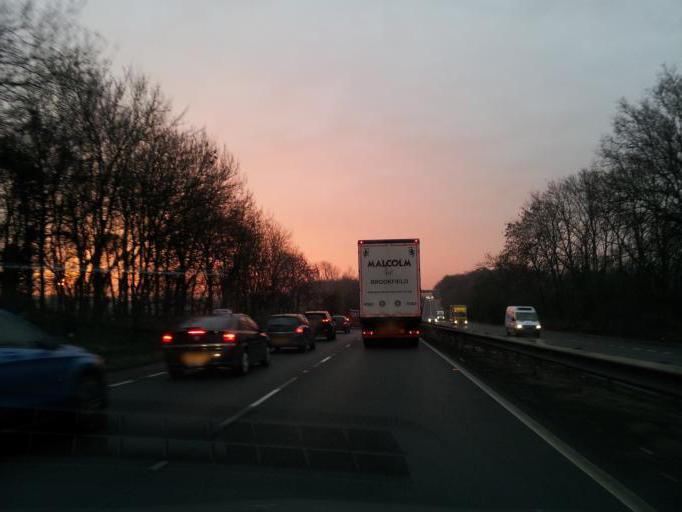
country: GB
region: England
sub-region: Peterborough
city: Thornhaugh
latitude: 52.5907
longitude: -0.4169
